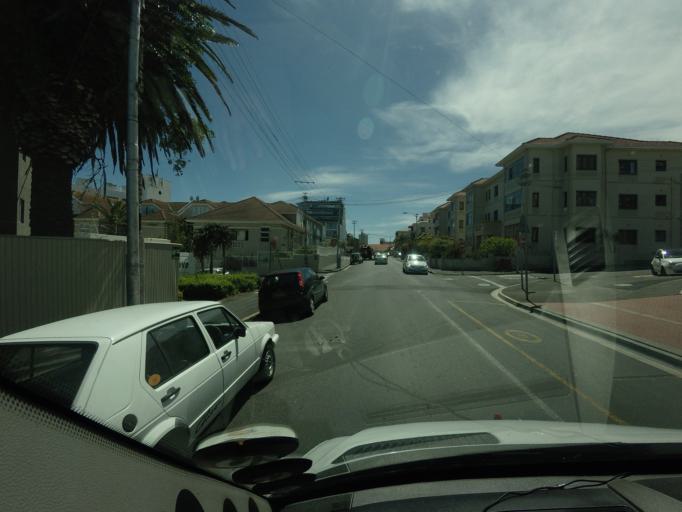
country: ZA
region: Western Cape
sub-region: City of Cape Town
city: Cape Town
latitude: -33.9243
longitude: 18.3796
